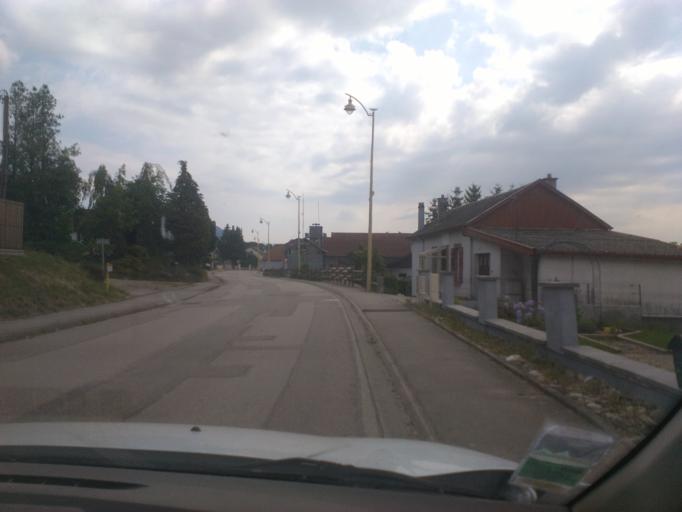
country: FR
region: Lorraine
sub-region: Departement des Vosges
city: Etival-Clairefontaine
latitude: 48.3635
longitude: 6.8573
